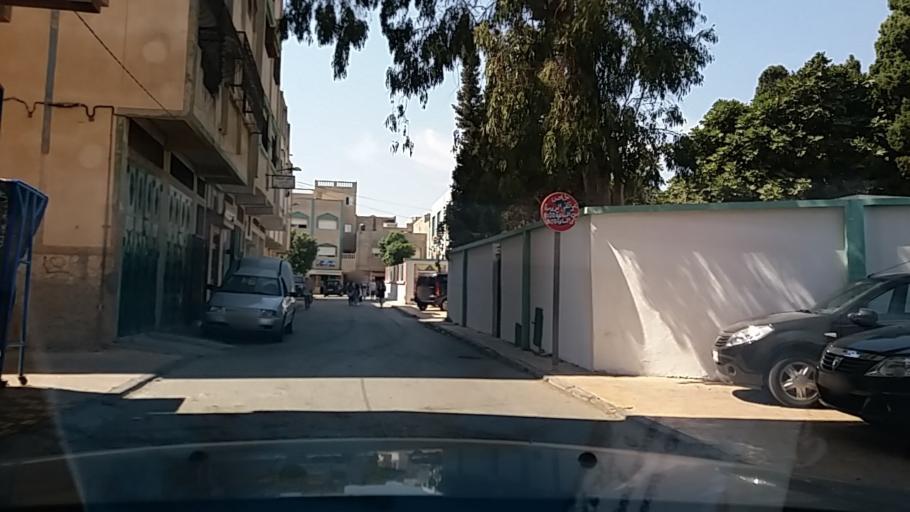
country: MA
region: Tanger-Tetouan
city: Tetouan
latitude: 35.5692
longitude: -5.4001
